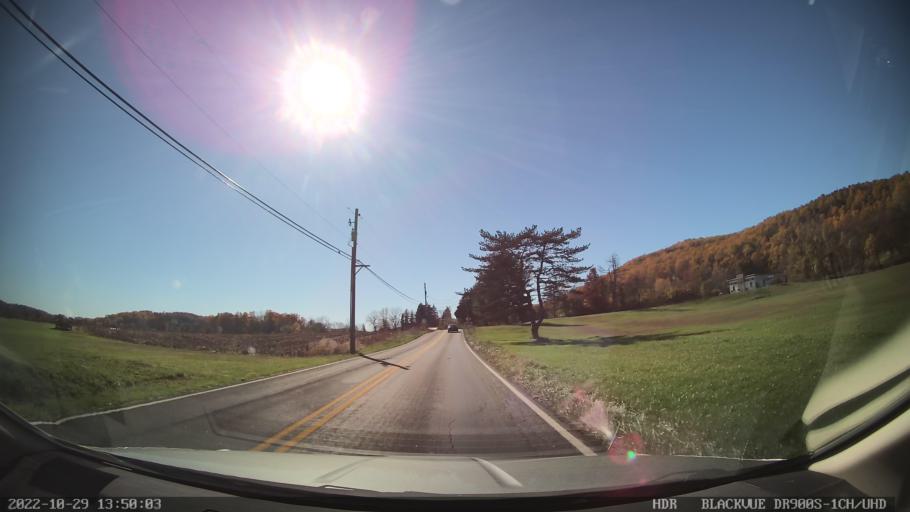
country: US
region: Pennsylvania
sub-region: Lehigh County
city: Emmaus
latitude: 40.5376
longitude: -75.4569
